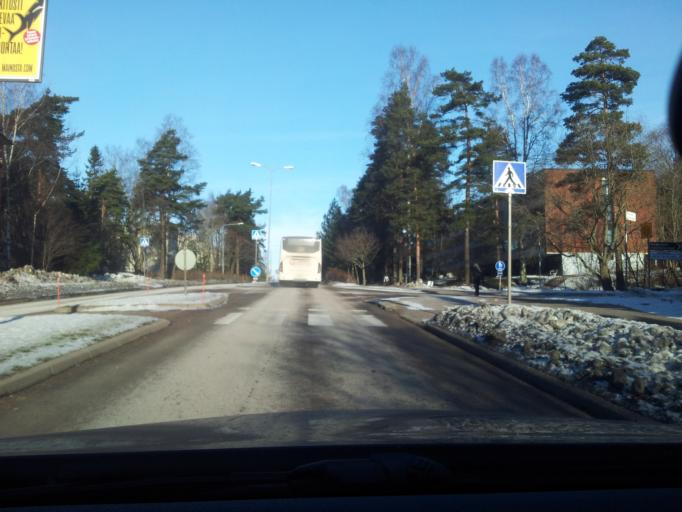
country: FI
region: Uusimaa
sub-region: Helsinki
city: Koukkuniemi
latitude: 60.1640
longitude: 24.7736
